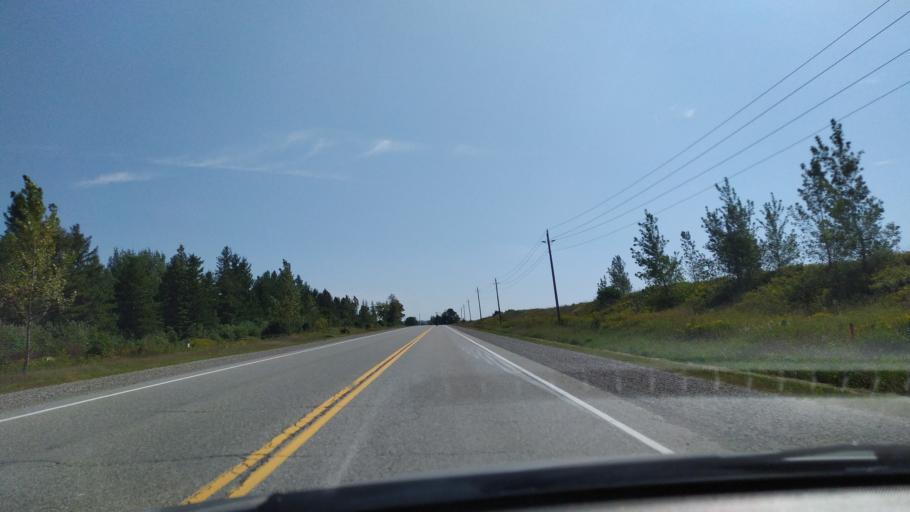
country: CA
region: Ontario
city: Ingersoll
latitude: 43.0794
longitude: -80.8618
